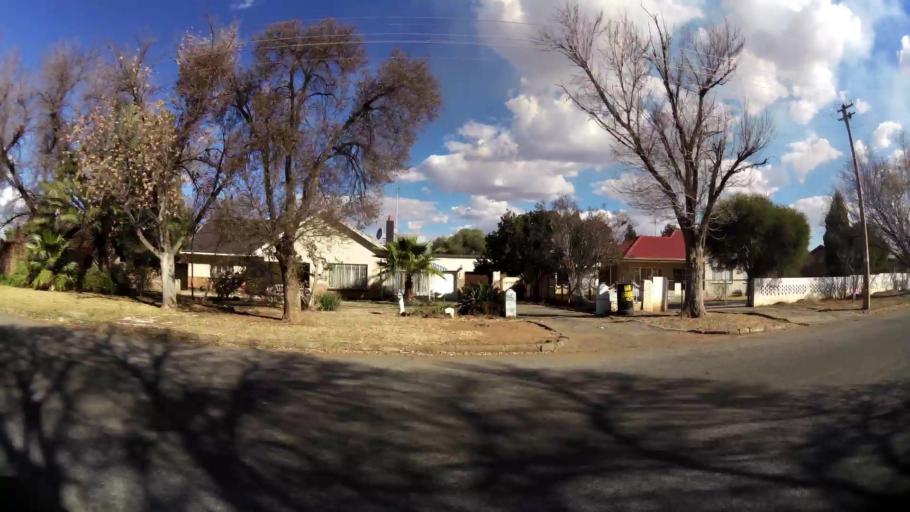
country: ZA
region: North-West
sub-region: Dr Kenneth Kaunda District Municipality
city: Klerksdorp
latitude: -26.8304
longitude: 26.6616
